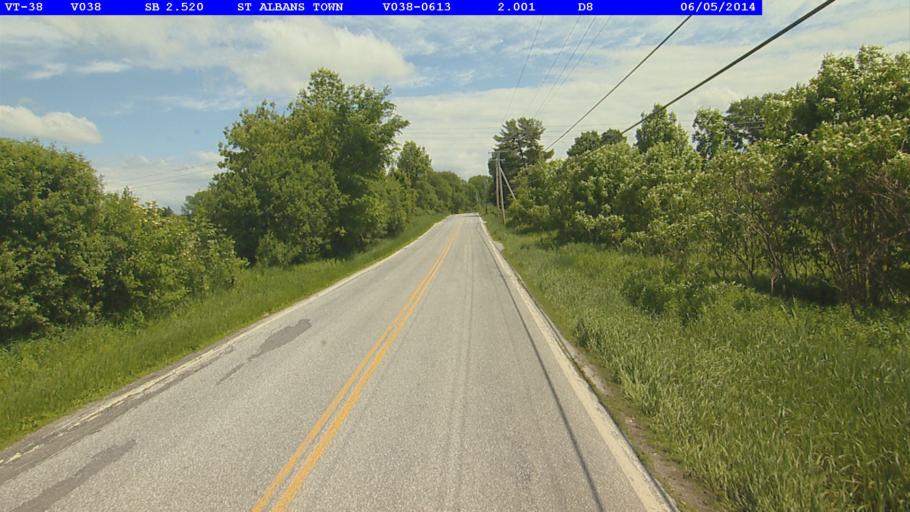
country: US
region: Vermont
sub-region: Franklin County
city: Saint Albans
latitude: 44.8468
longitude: -73.1129
